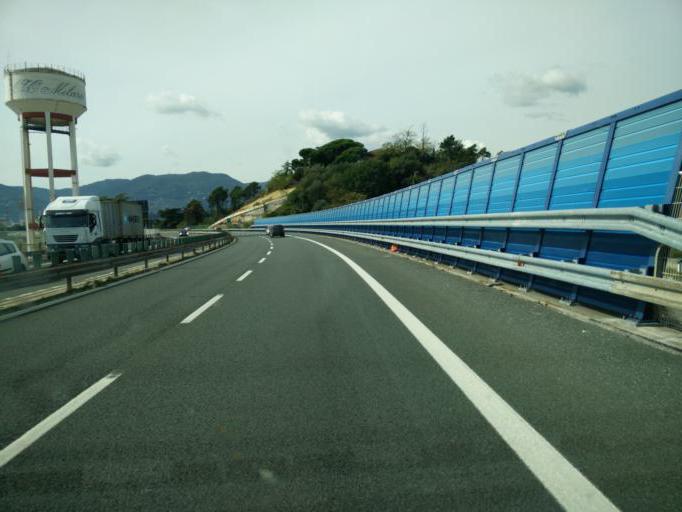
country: IT
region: Liguria
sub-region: Provincia di La Spezia
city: Pitelli
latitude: 44.1151
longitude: 9.8659
